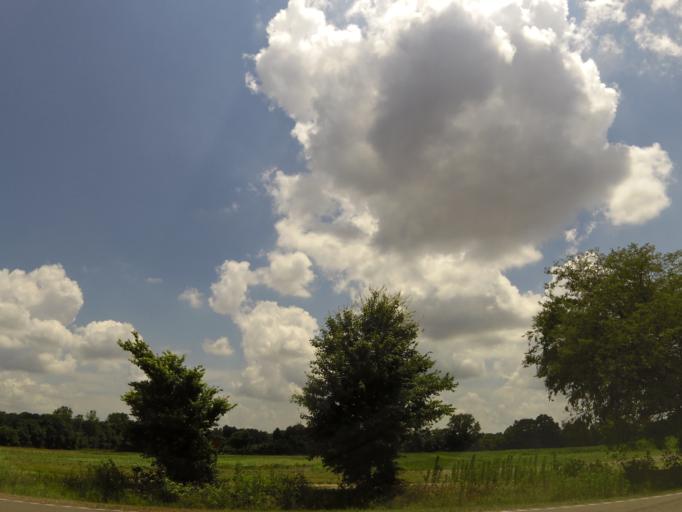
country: US
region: Tennessee
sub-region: Dyer County
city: Dyersburg
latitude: 36.0251
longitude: -89.3429
